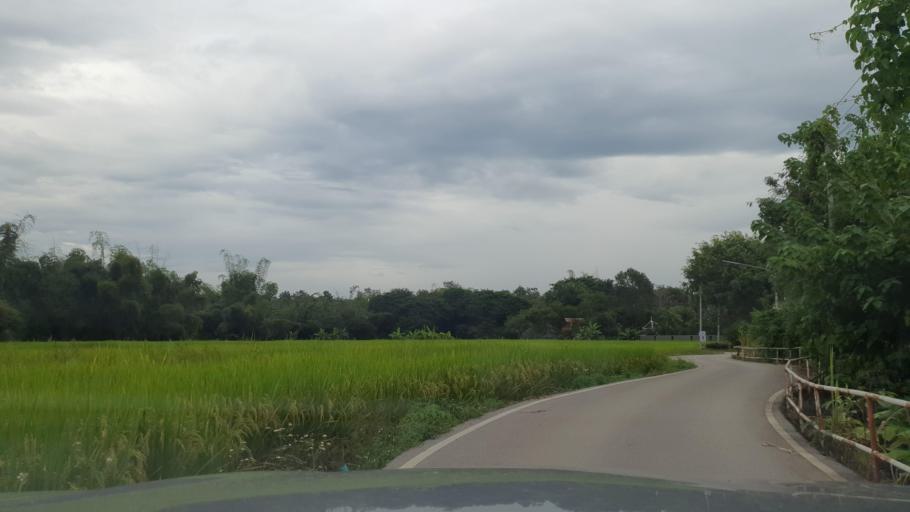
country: TH
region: Chiang Mai
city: San Sai
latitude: 18.9306
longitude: 98.9208
